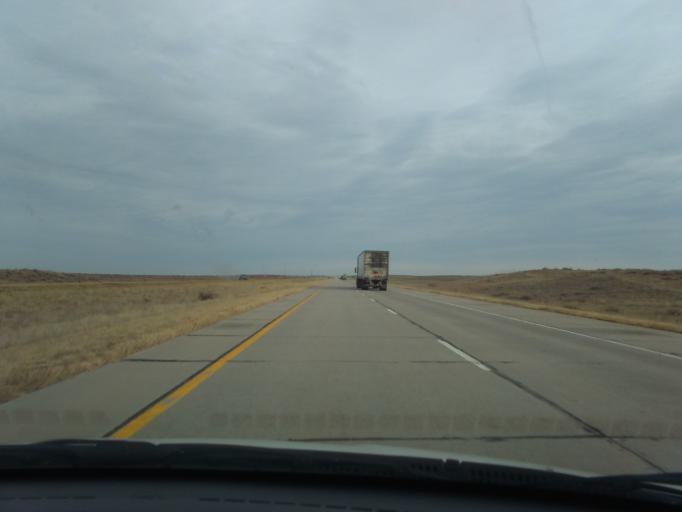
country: US
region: Colorado
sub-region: Weld County
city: Keenesburg
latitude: 40.2104
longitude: -104.2302
